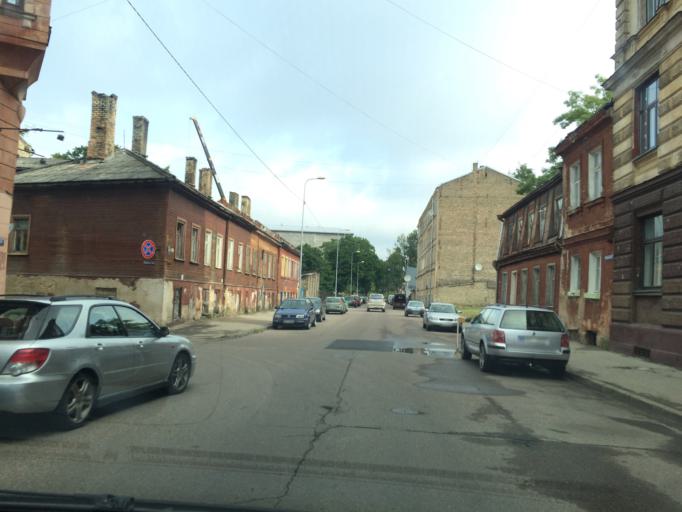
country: LV
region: Riga
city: Riga
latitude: 56.9442
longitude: 24.1345
